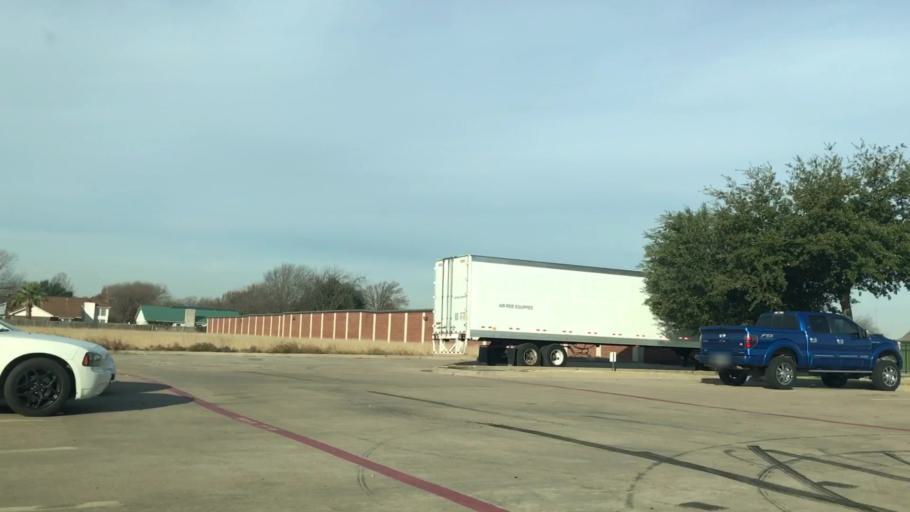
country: US
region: Texas
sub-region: Tarrant County
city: Watauga
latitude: 32.8622
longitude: -97.2914
